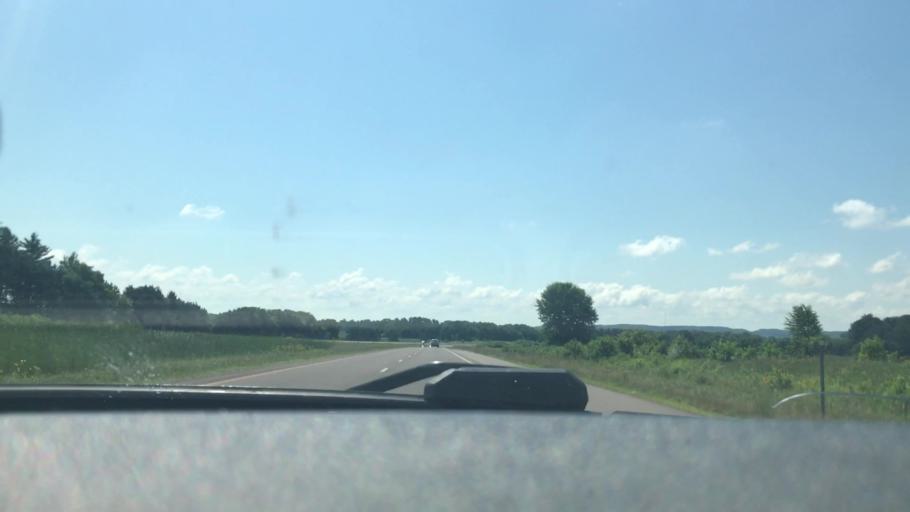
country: US
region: Wisconsin
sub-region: Chippewa County
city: Bloomer
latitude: 45.0267
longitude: -91.4469
